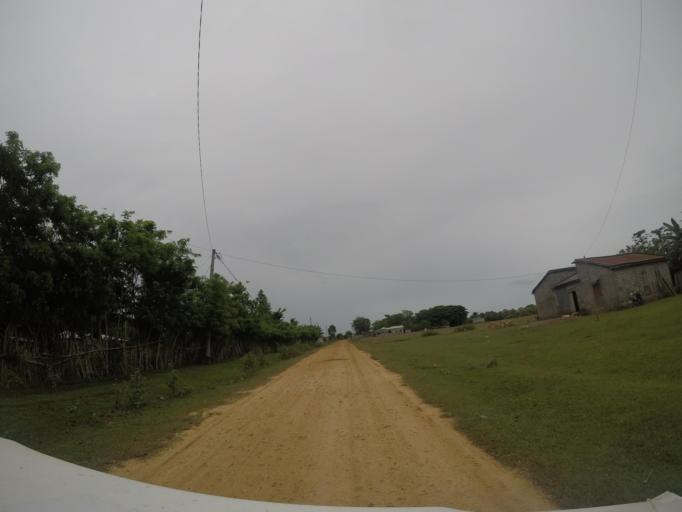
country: TL
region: Lautem
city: Lospalos
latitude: -8.5277
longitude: 127.0117
